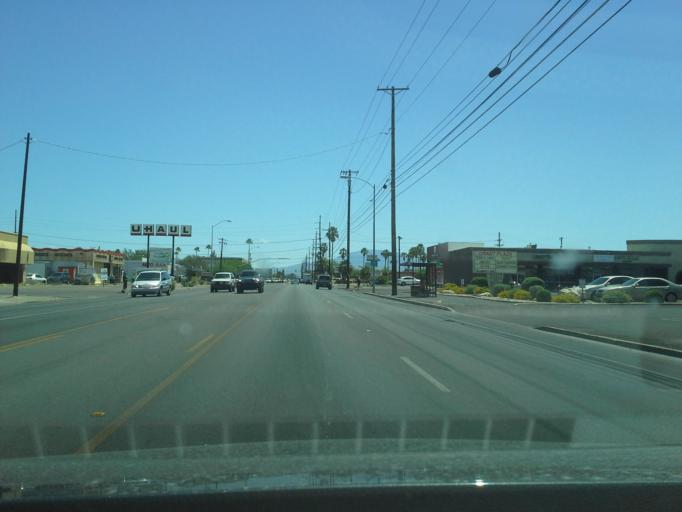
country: US
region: Arizona
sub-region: Pima County
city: Tucson
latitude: 32.2505
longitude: -110.9181
